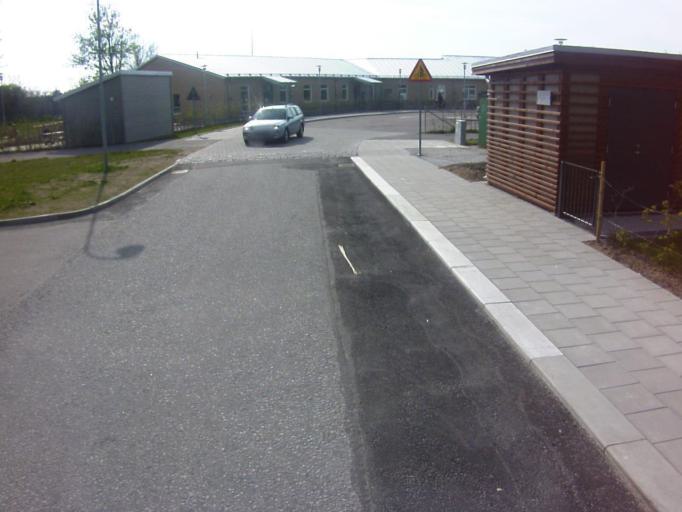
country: SE
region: Skane
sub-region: Kavlinge Kommun
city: Loddekopinge
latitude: 55.7614
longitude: 13.0094
